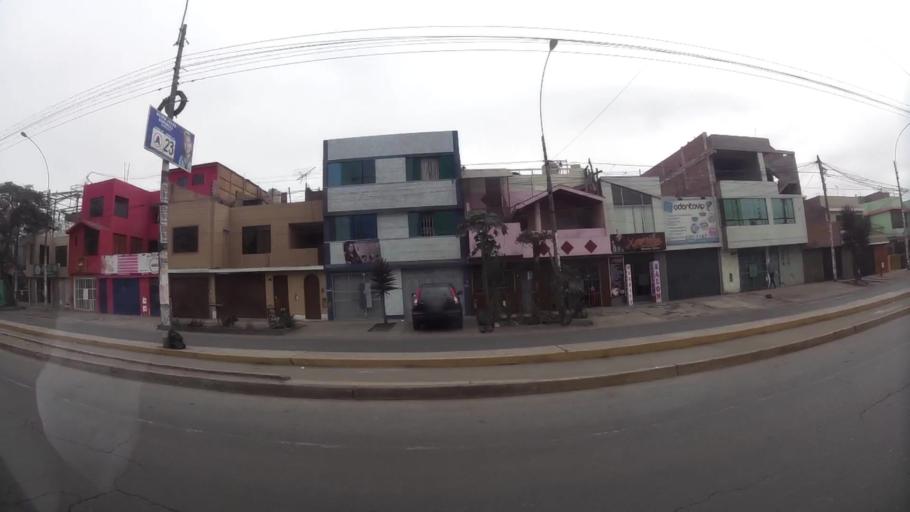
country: PE
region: Lima
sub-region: Lima
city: Independencia
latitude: -12.0004
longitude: -77.0840
